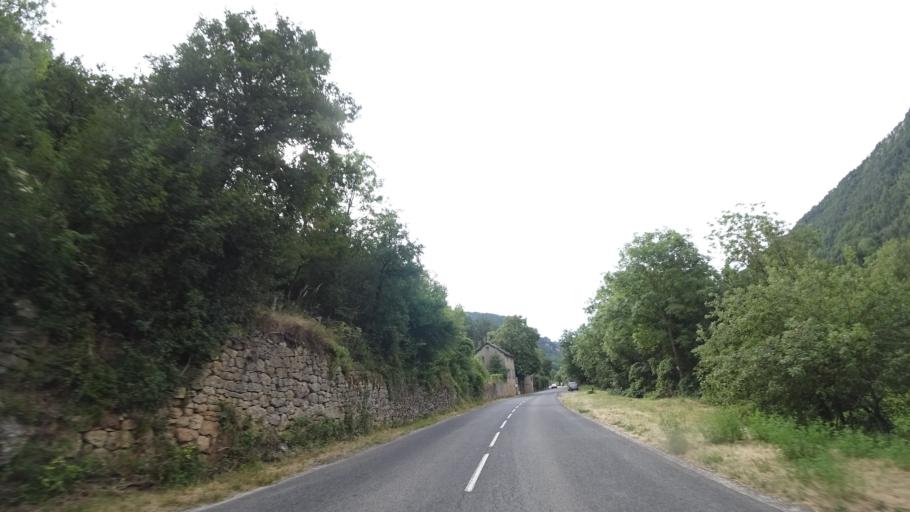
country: FR
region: Languedoc-Roussillon
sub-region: Departement de la Lozere
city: La Canourgue
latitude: 44.4188
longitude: 3.2293
